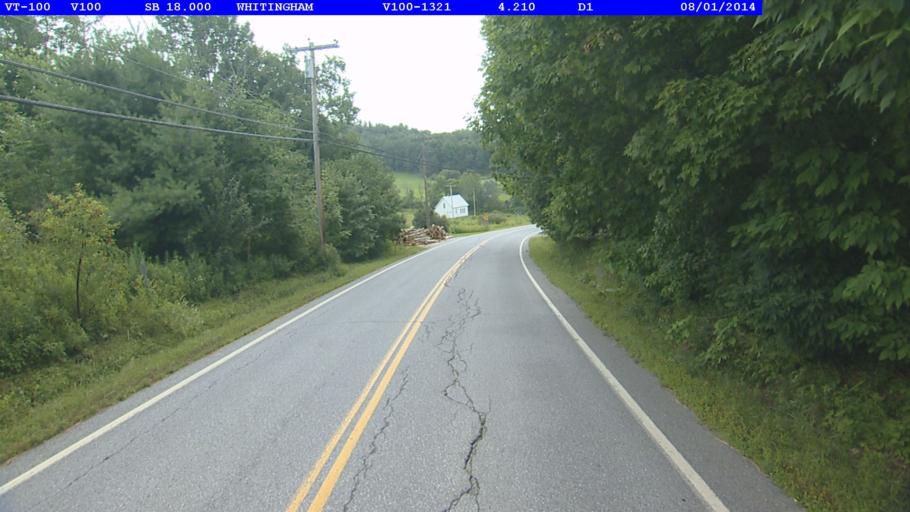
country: US
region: Massachusetts
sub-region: Franklin County
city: Charlemont
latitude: 42.7888
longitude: -72.8819
